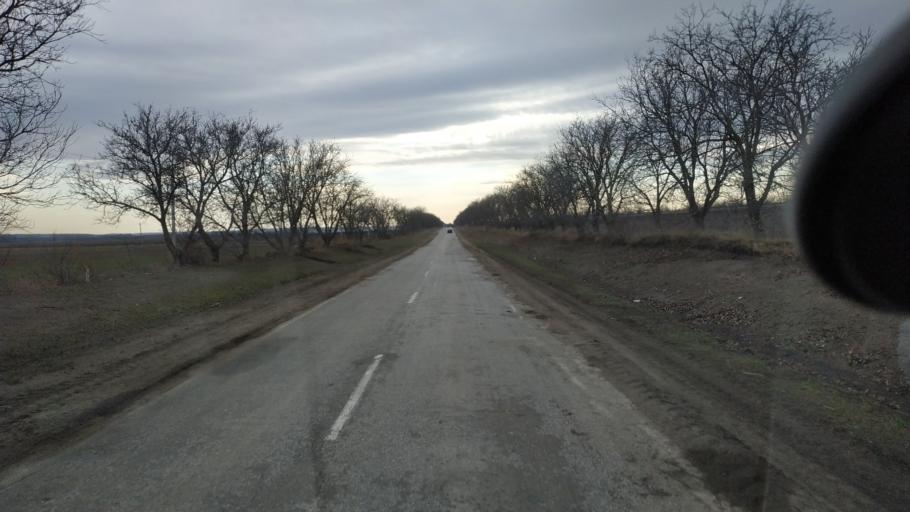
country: MD
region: Criuleni
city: Criuleni
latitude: 47.1875
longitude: 29.1429
